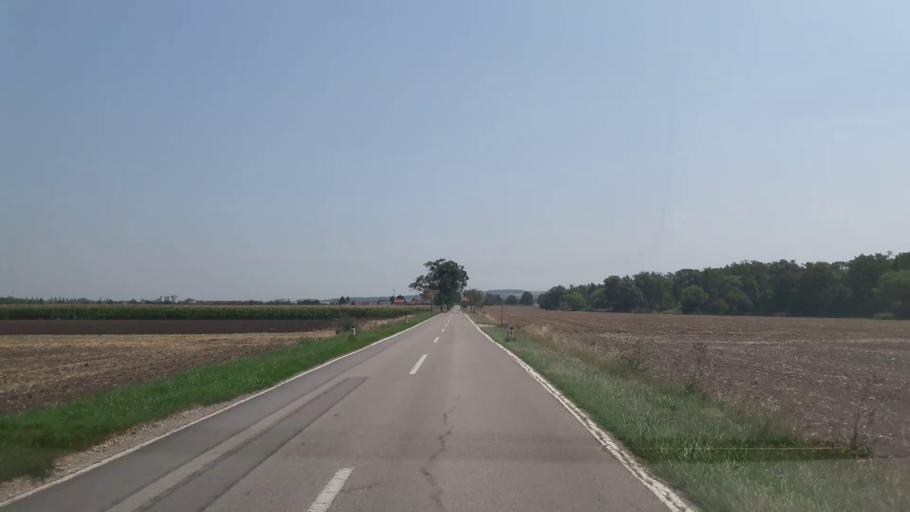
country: AT
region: Lower Austria
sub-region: Politischer Bezirk Bruck an der Leitha
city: Bruck an der Leitha
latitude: 48.0165
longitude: 16.7066
